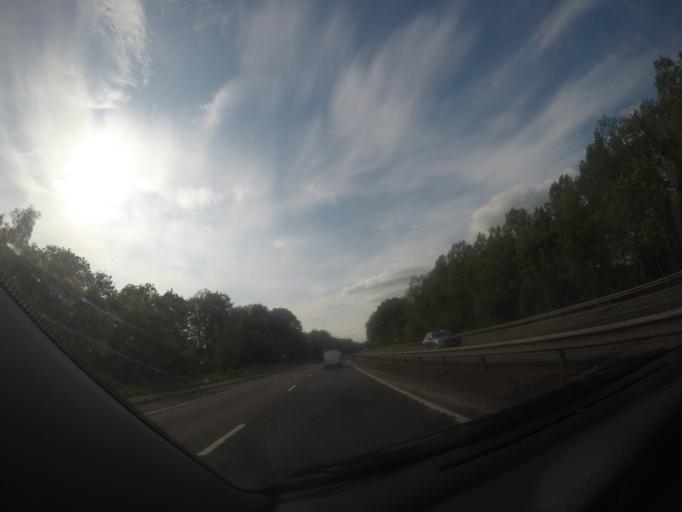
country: GB
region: Scotland
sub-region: North Lanarkshire
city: Motherwell
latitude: 55.7694
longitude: -4.0053
